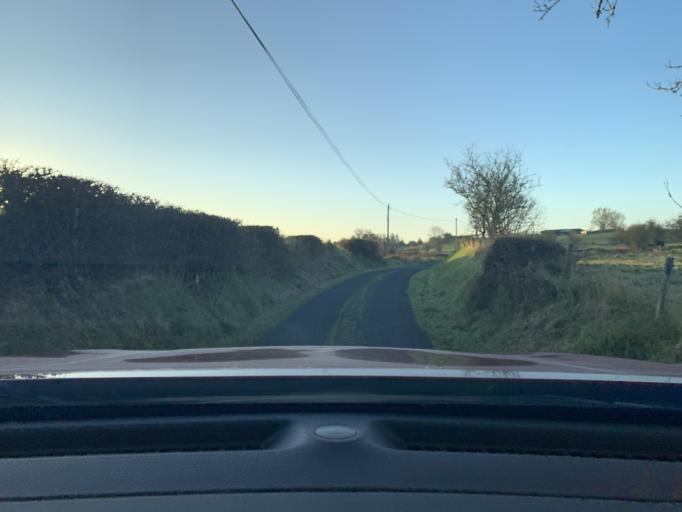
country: IE
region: Connaught
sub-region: Sligo
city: Ballymote
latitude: 54.0713
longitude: -8.5494
